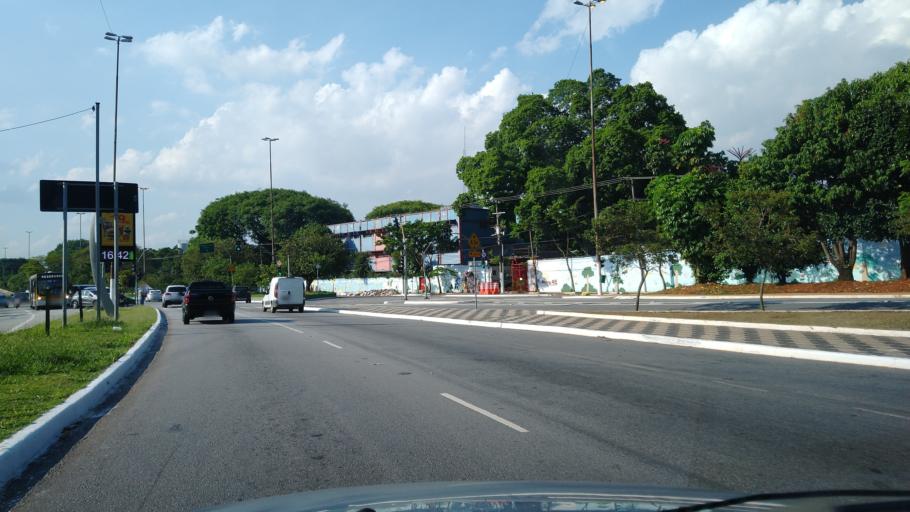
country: BR
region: Sao Paulo
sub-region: Sao Paulo
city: Sao Paulo
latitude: -23.5521
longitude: -46.5999
